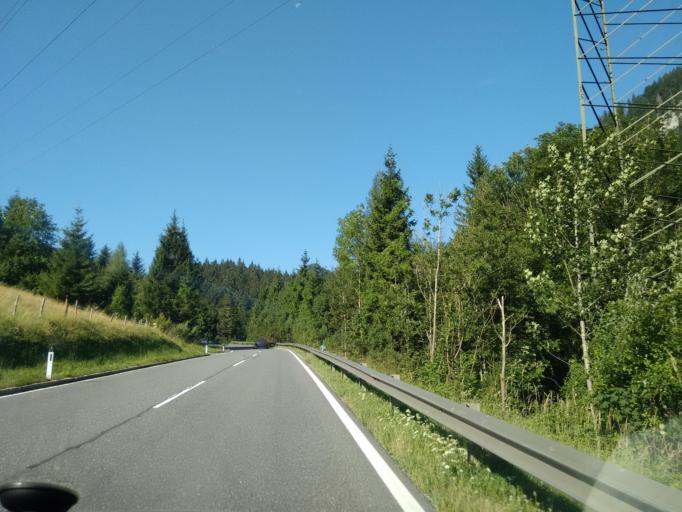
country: AT
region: Styria
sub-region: Politischer Bezirk Liezen
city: Ardning
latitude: 47.6355
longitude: 14.3282
